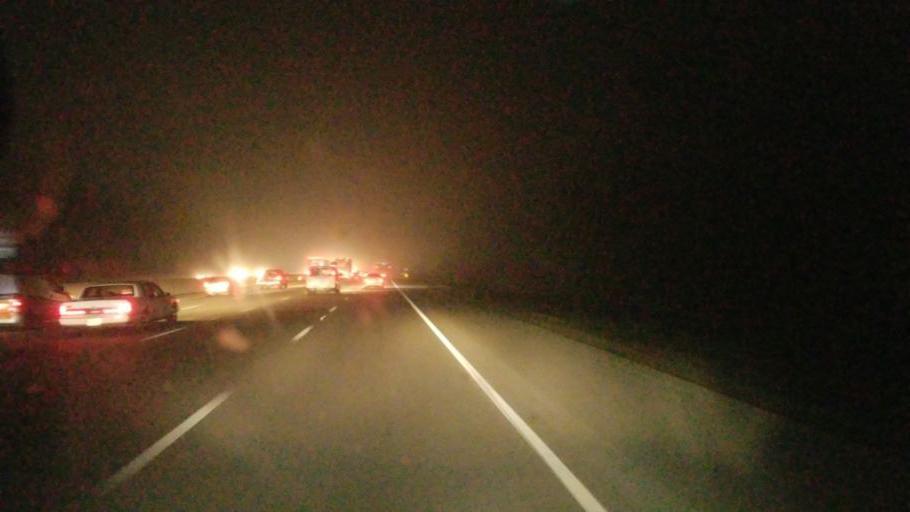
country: US
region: Ohio
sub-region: Franklin County
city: Obetz
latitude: 39.8824
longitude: -83.0215
